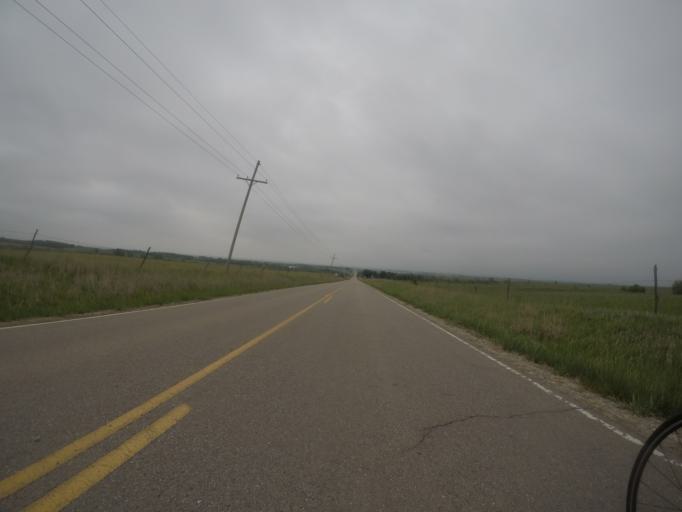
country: US
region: Kansas
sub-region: Pottawatomie County
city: Westmoreland
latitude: 39.5222
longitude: -96.2746
